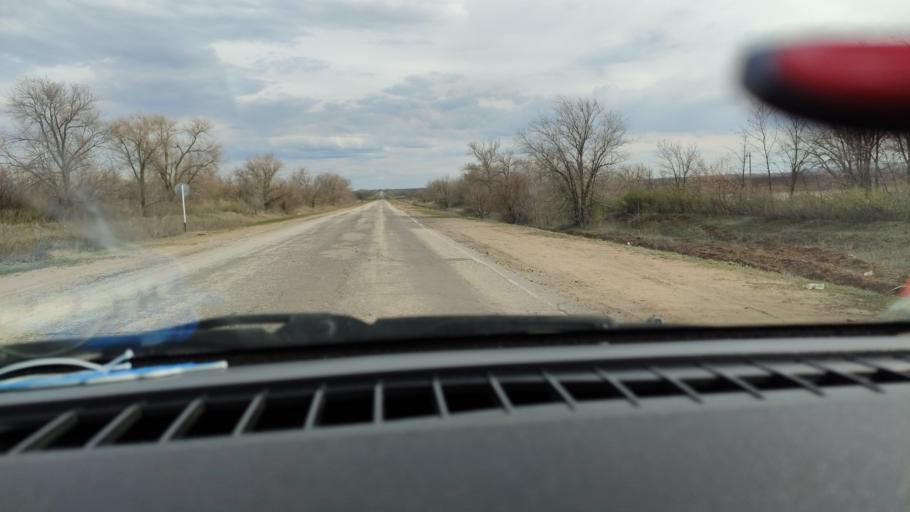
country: RU
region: Saratov
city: Rovnoye
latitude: 51.0131
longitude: 46.0971
